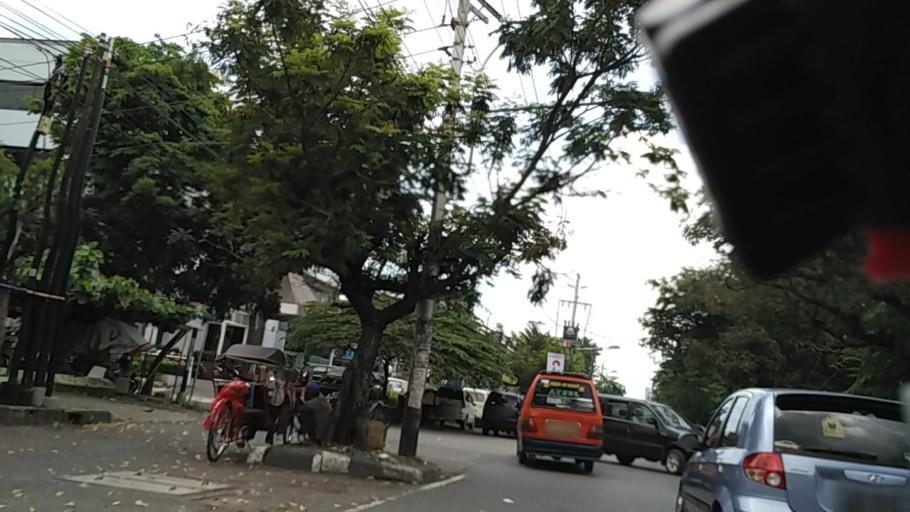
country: ID
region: Central Java
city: Semarang
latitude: -6.9965
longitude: 110.4320
